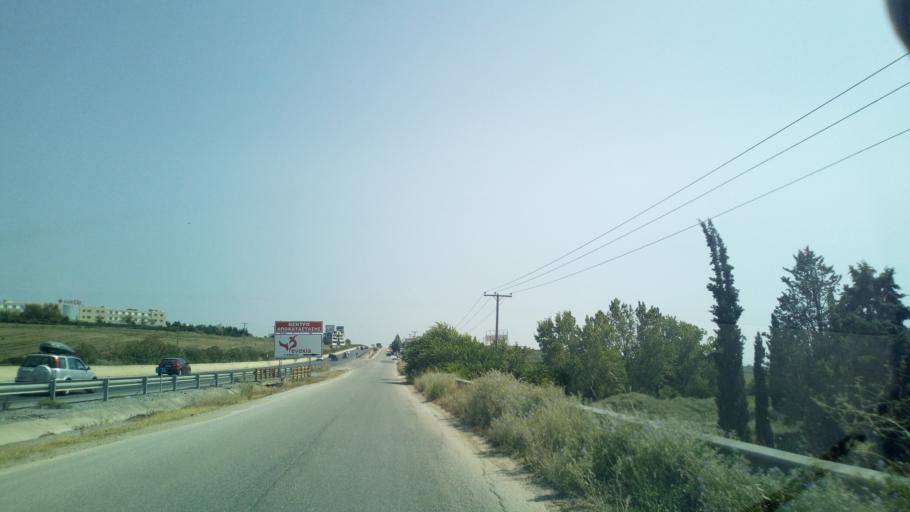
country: GR
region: Central Macedonia
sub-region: Nomos Chalkidikis
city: Lakkoma
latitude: 40.3610
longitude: 23.0511
